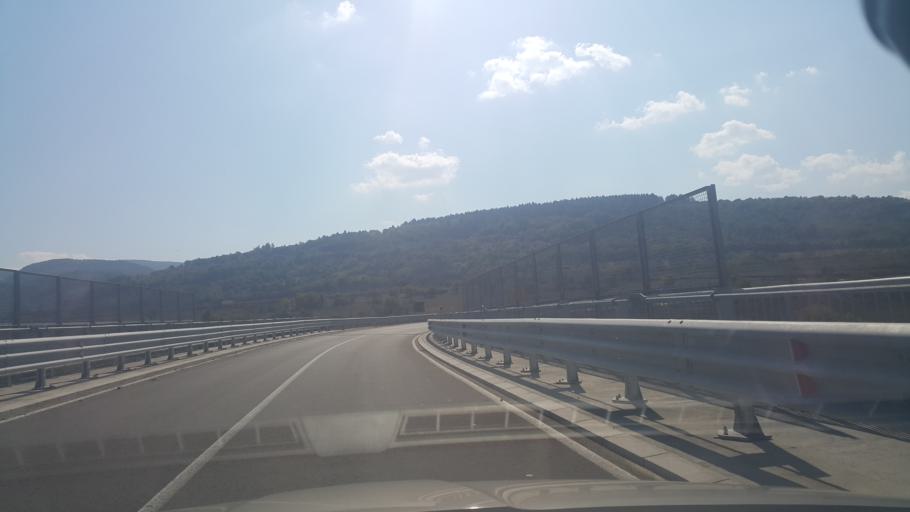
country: RS
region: Central Serbia
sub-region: Pirotski Okrug
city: Bela Palanka
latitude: 43.2285
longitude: 22.3907
